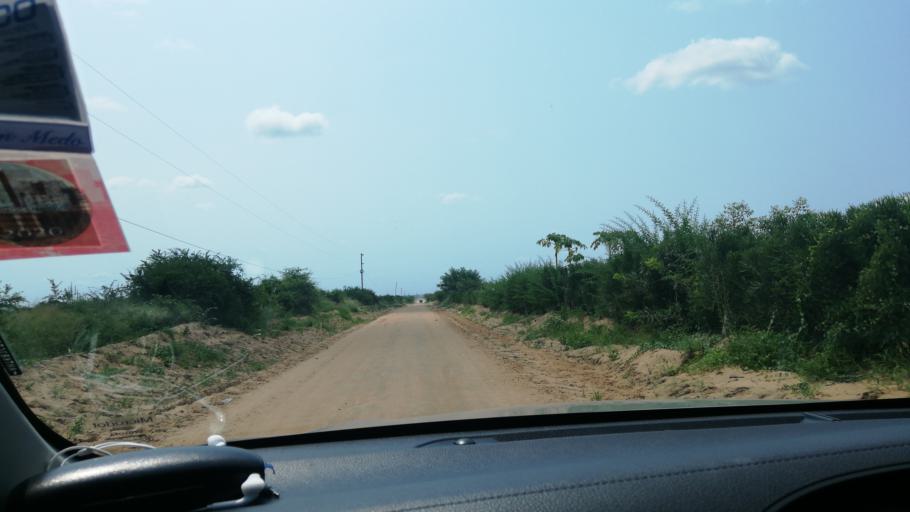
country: MZ
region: Maputo
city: Matola
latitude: -26.0959
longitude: 32.3895
